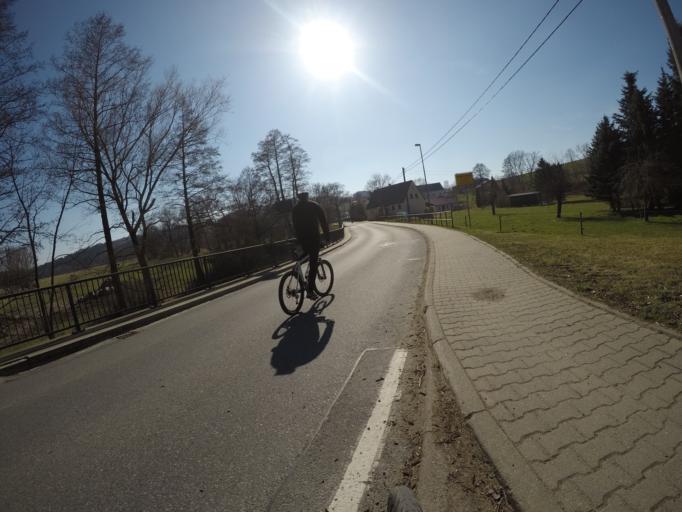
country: DE
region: Saxony
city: Lichtenberg
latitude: 50.8412
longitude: 13.4016
